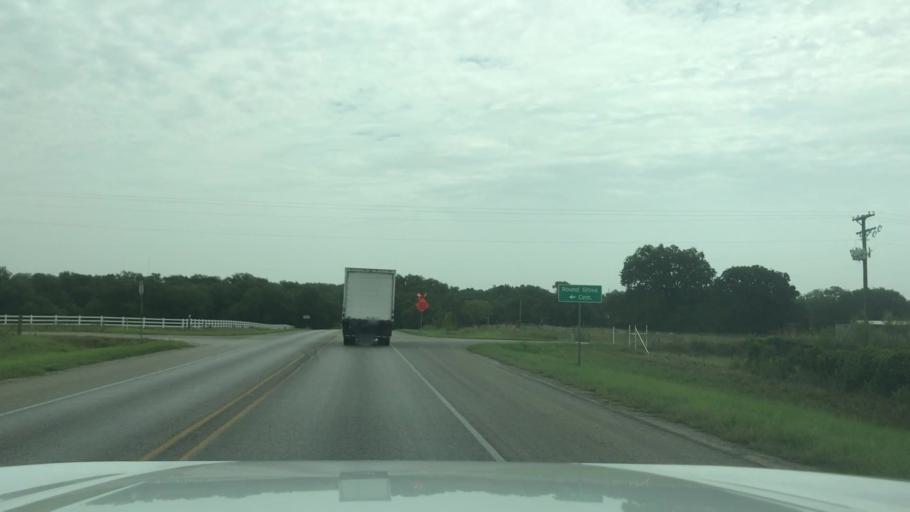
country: US
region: Texas
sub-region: Comanche County
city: De Leon
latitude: 32.1041
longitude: -98.4852
